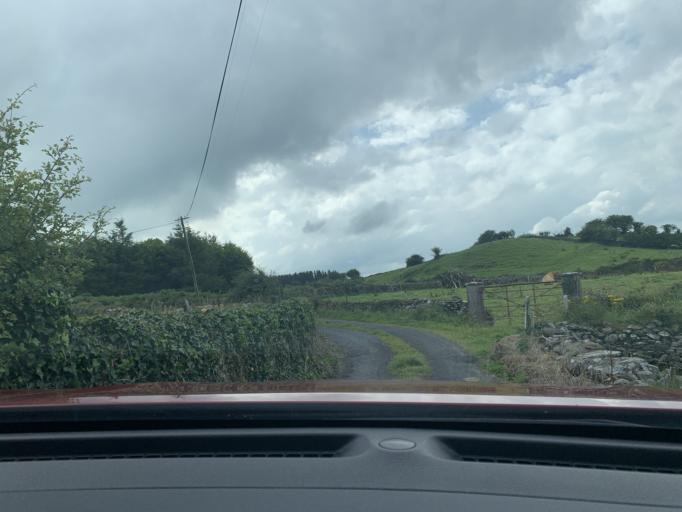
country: IE
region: Connaught
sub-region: Maigh Eo
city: Kiltamagh
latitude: 53.8419
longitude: -9.0073
